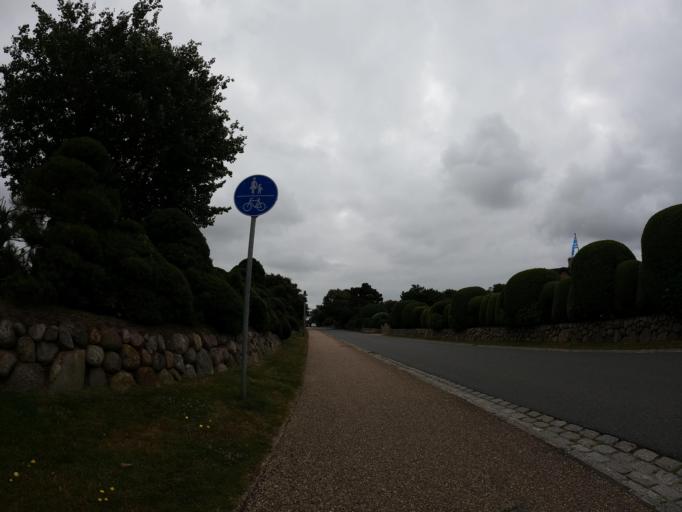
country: DE
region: Schleswig-Holstein
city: Tinnum
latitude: 54.9521
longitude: 8.3441
